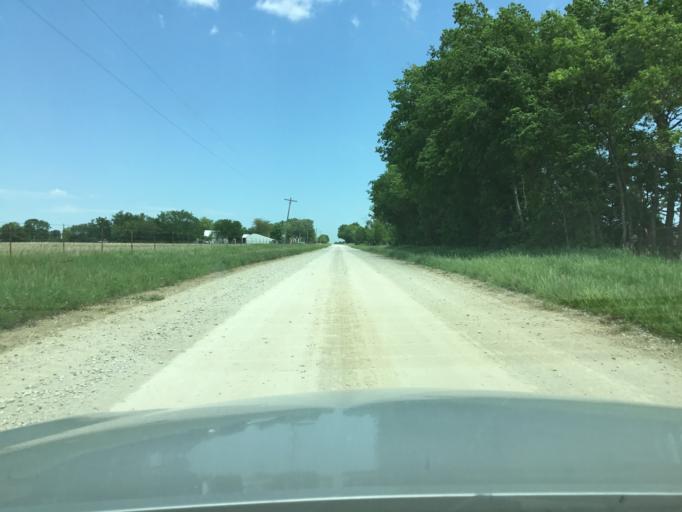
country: US
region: Kansas
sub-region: Montgomery County
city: Independence
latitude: 37.0986
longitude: -95.7829
